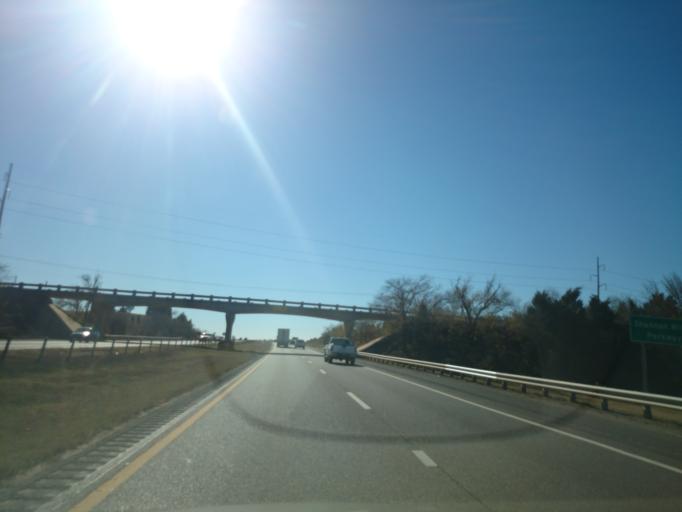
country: US
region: Oklahoma
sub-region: Oklahoma County
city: Edmond
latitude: 35.6682
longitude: -97.4214
